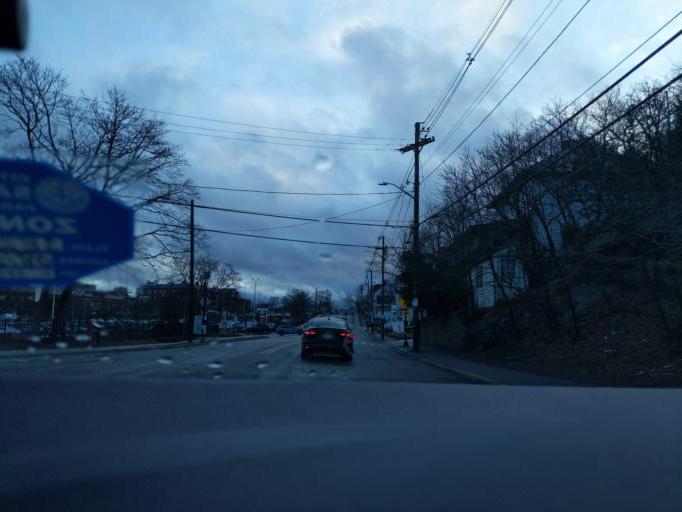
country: US
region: Massachusetts
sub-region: Essex County
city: Salem
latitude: 42.5143
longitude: -70.9064
